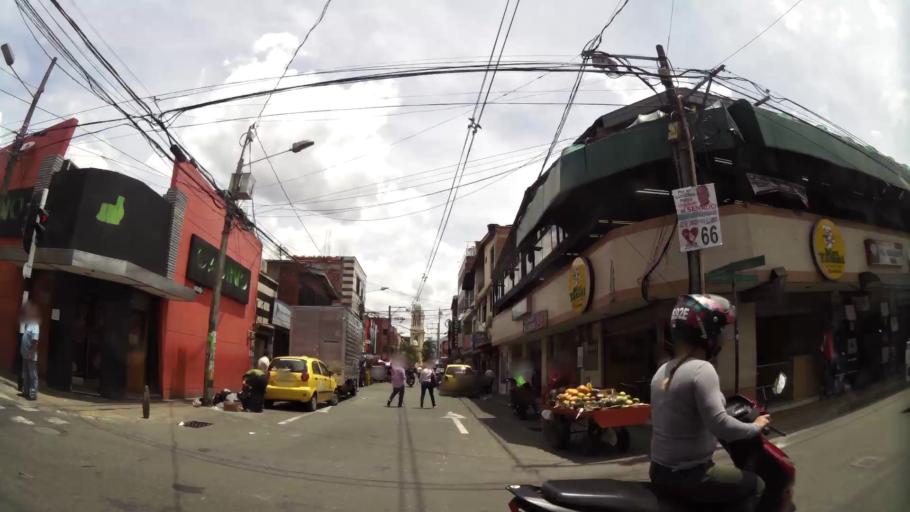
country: CO
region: Antioquia
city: Bello
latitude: 6.3341
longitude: -75.5564
